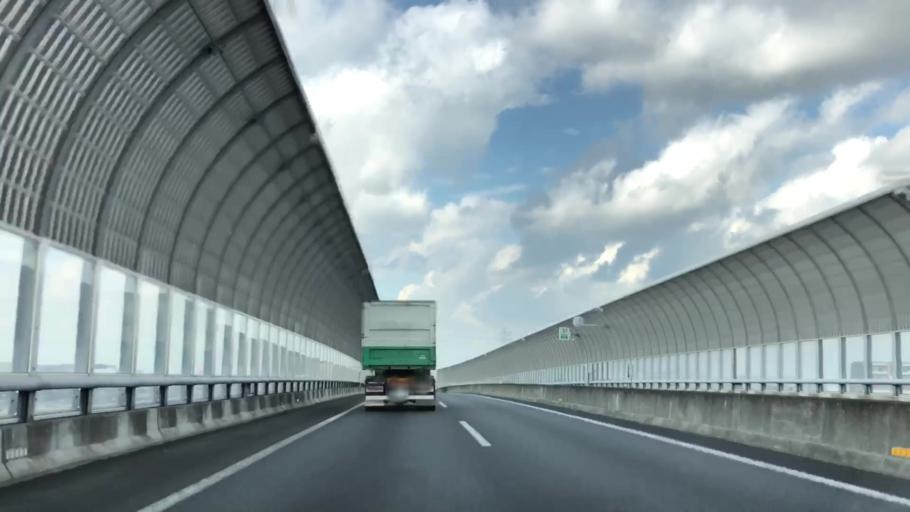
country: JP
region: Saitama
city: Yashio-shi
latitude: 35.8180
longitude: 139.8743
